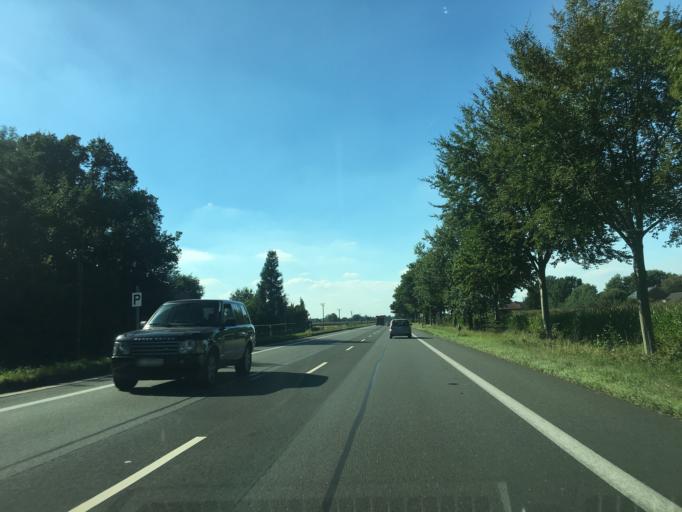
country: DE
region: North Rhine-Westphalia
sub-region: Regierungsbezirk Munster
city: Beelen
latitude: 51.9209
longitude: 8.1453
